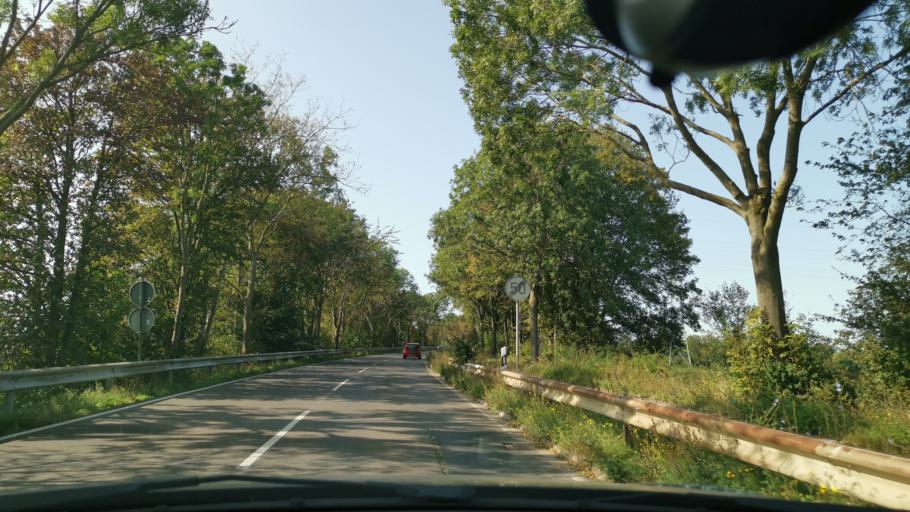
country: DE
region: North Rhine-Westphalia
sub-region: Regierungsbezirk Dusseldorf
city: Grevenbroich
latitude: 51.1186
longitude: 6.5986
